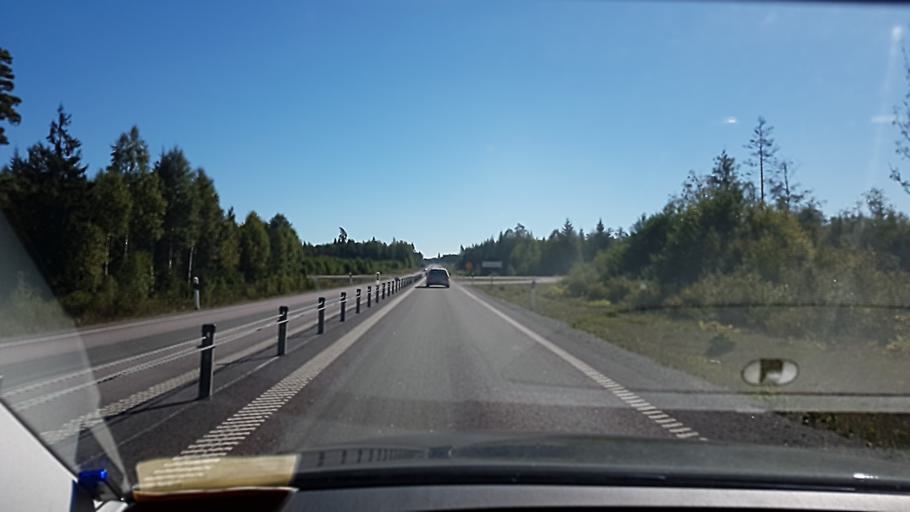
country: SE
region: Kalmar
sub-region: Emmaboda Kommun
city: Emmaboda
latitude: 56.7320
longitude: 15.5418
